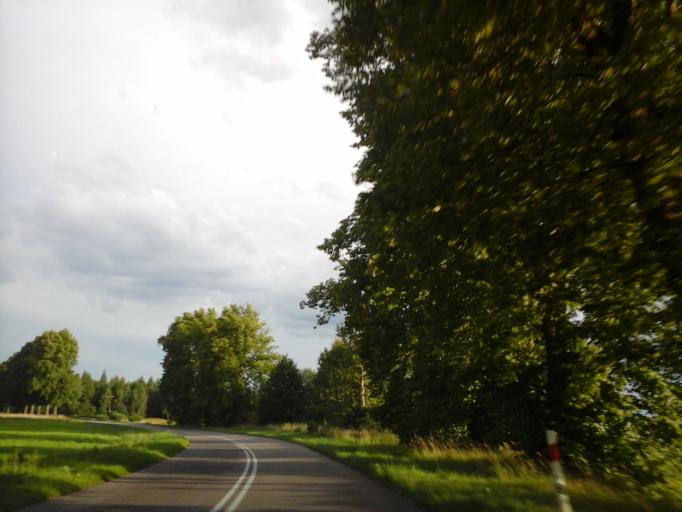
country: PL
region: West Pomeranian Voivodeship
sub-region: Powiat kamienski
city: Golczewo
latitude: 53.7474
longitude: 15.0104
